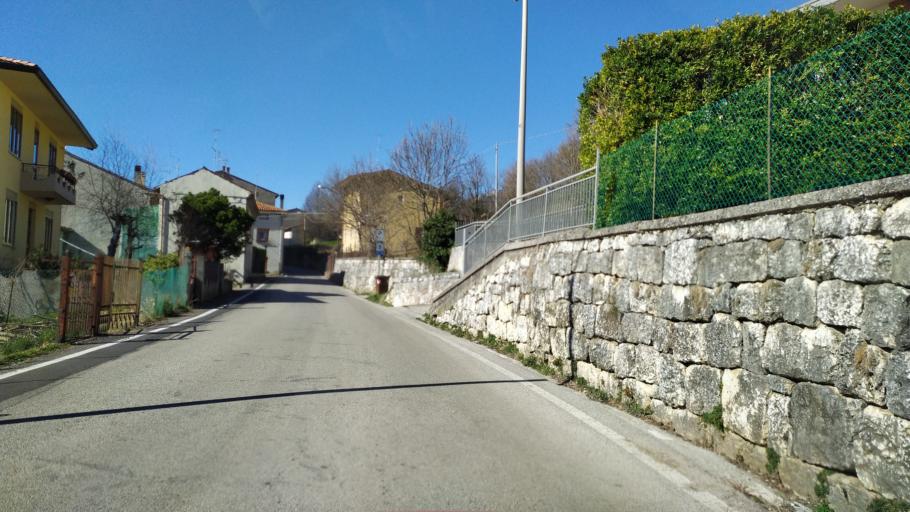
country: IT
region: Veneto
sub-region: Provincia di Vicenza
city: Chiuppano
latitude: 45.7677
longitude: 11.4691
